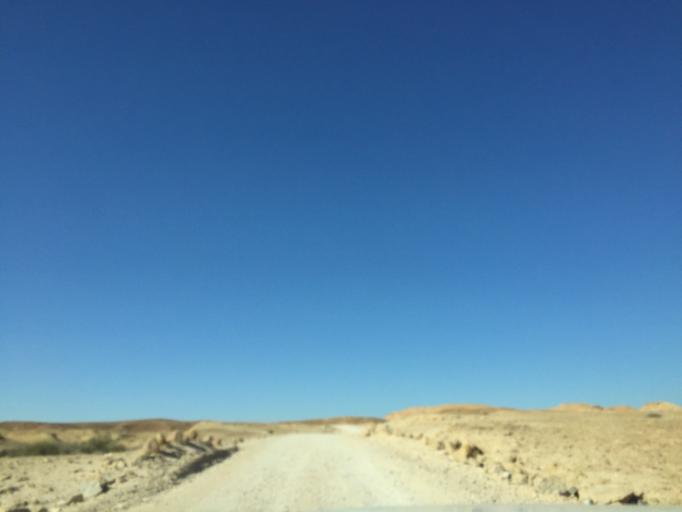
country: IL
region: Southern District
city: Mitzpe Ramon
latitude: 30.6091
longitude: 34.9367
